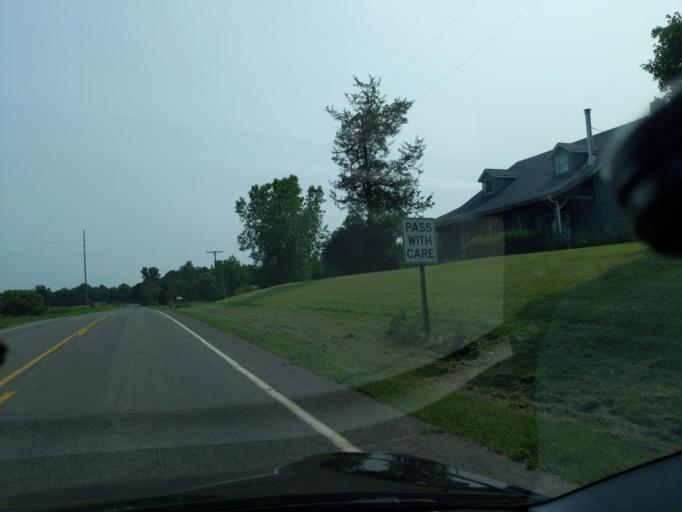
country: US
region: Michigan
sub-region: Eaton County
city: Eaton Rapids
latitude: 42.5184
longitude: -84.5618
